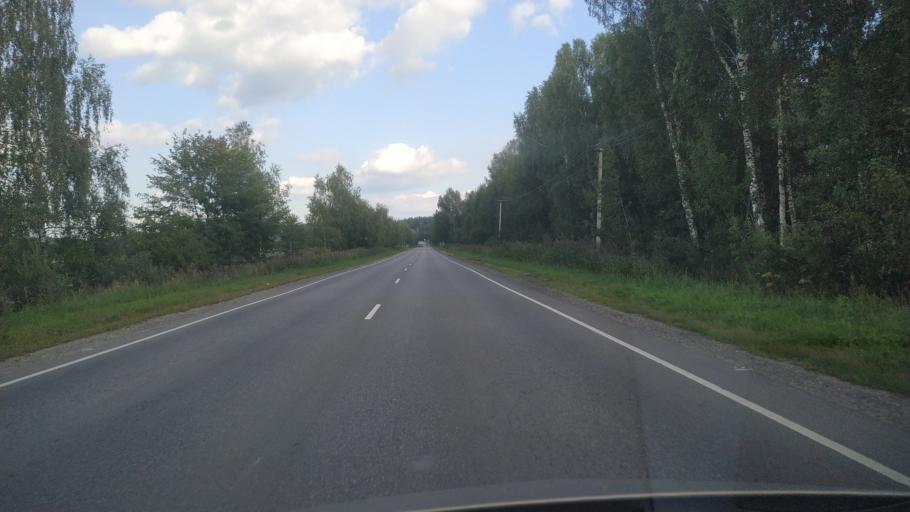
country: RU
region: Moskovskaya
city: Vereya
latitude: 55.7056
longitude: 39.1539
